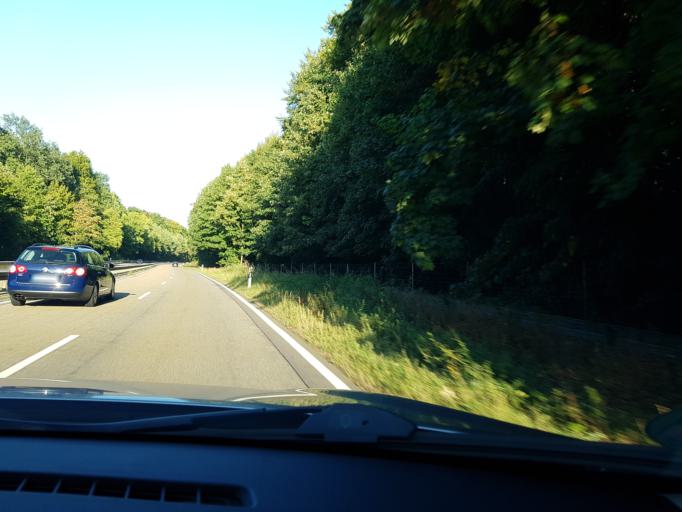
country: DE
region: Rheinland-Pfalz
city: Miellen
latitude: 50.3485
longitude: 7.6554
